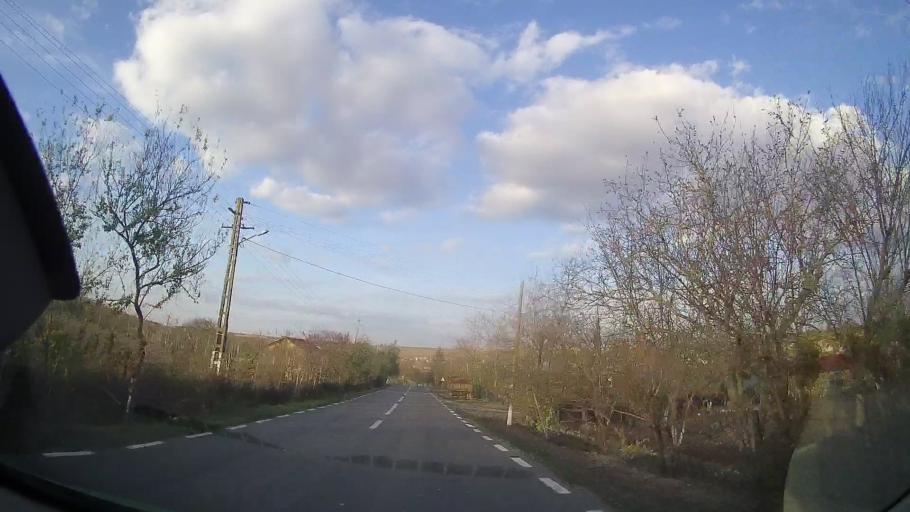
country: RO
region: Constanta
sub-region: Comuna Independenta
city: Independenta
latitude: 43.9522
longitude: 28.0751
